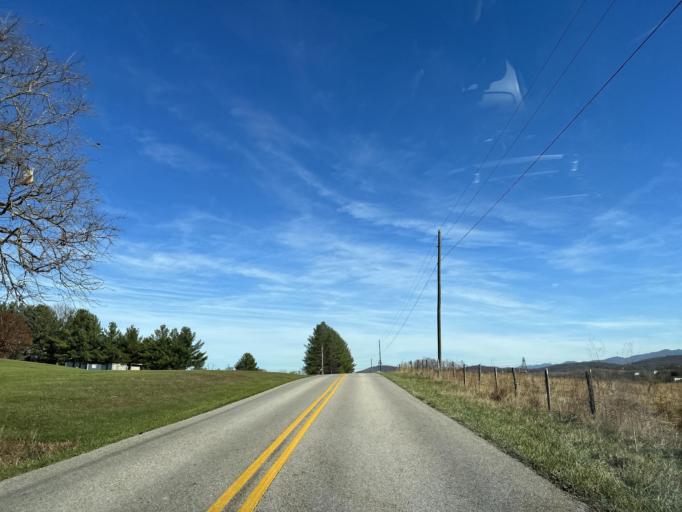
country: US
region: Virginia
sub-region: Augusta County
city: Fishersville
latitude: 38.1510
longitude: -78.9305
